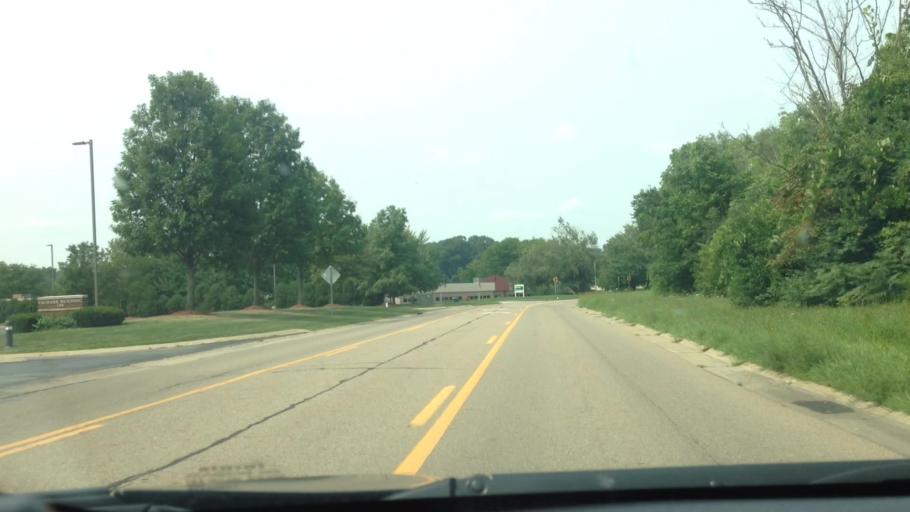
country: US
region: Ohio
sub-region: Summit County
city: Montrose-Ghent
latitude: 41.1387
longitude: -81.6462
